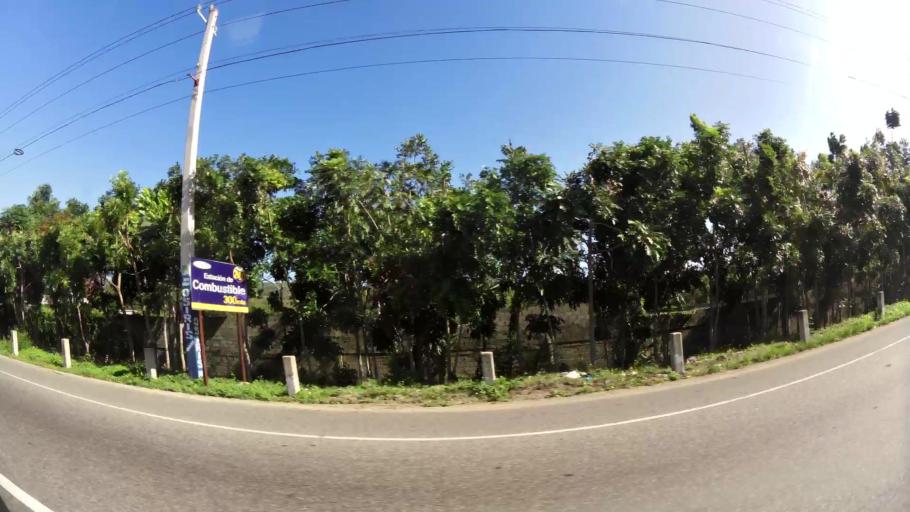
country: DO
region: San Cristobal
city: San Cristobal
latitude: 18.4311
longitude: -70.1034
